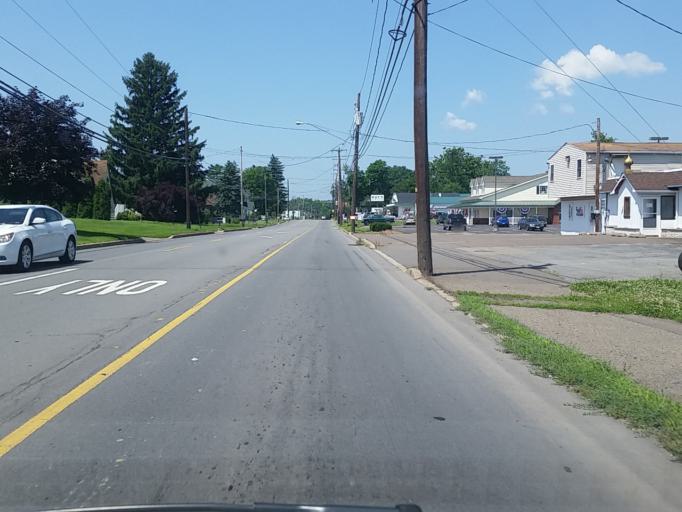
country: US
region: Pennsylvania
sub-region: Columbia County
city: Mifflinville
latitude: 41.0469
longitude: -76.2751
